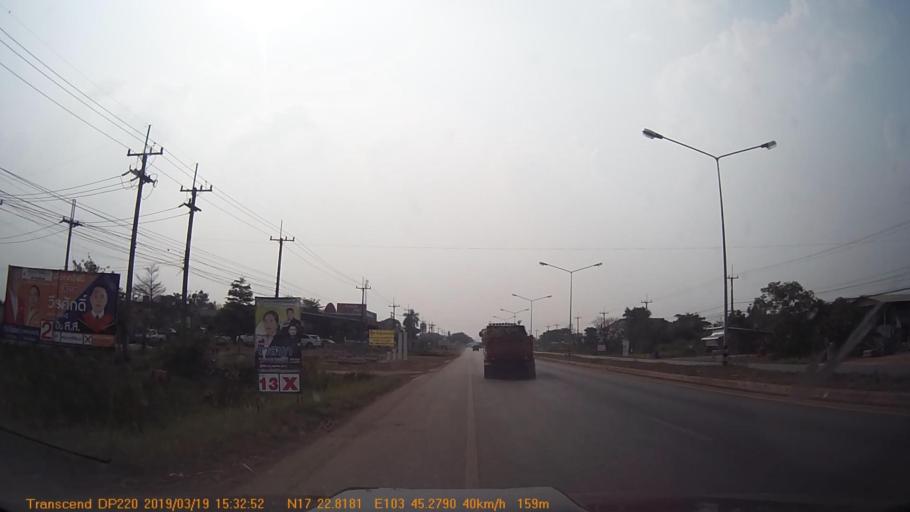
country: TH
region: Sakon Nakhon
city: Phang Khon
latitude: 17.3804
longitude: 103.7544
